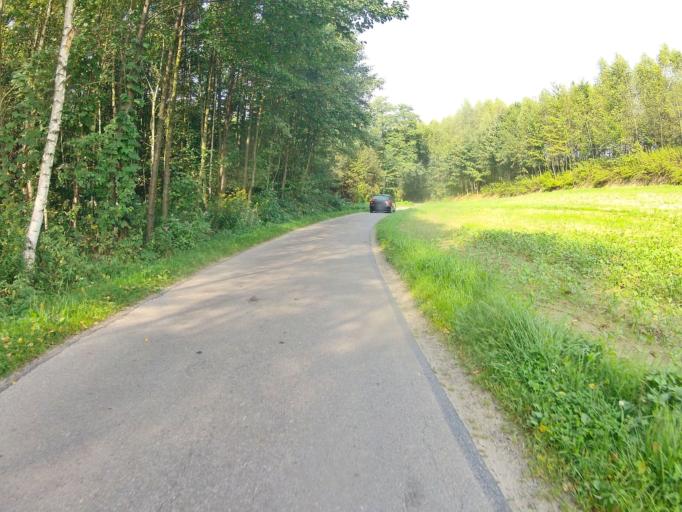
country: PL
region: Subcarpathian Voivodeship
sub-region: Powiat jasielski
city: Brzyska
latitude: 49.7921
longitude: 21.3918
